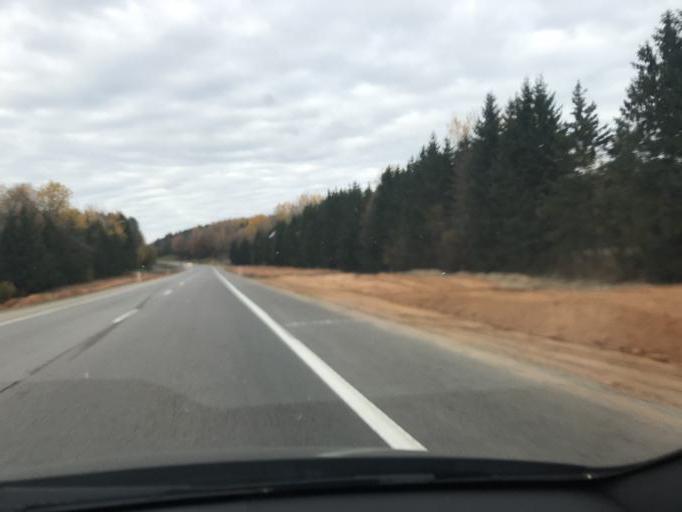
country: BY
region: Minsk
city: Slabada
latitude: 54.0352
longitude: 27.8440
